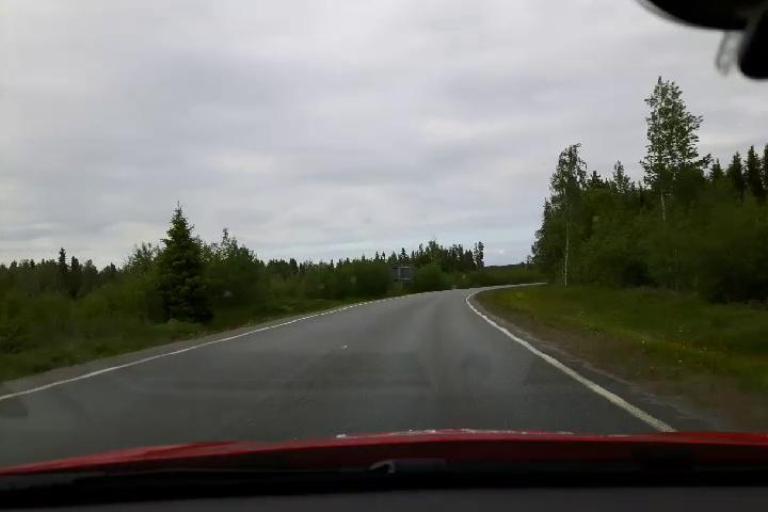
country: SE
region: Jaemtland
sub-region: Bergs Kommun
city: Hoverberg
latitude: 62.9162
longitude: 14.3281
